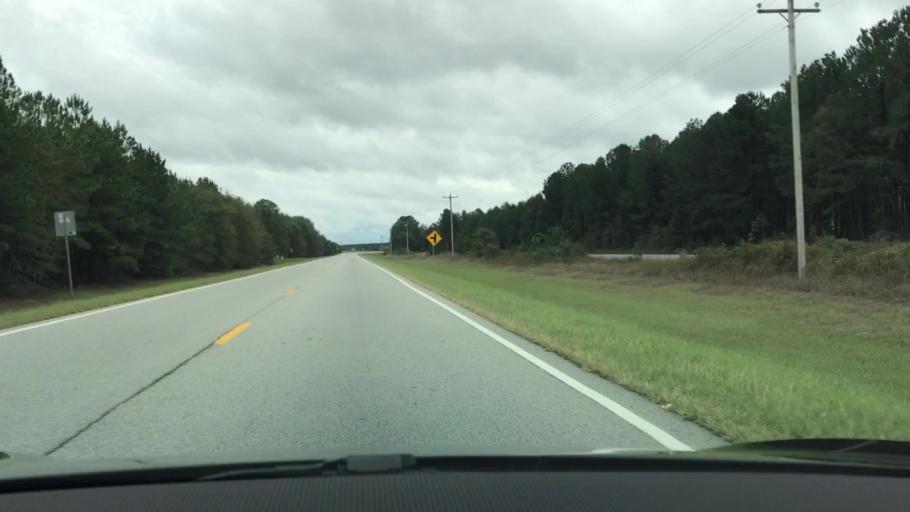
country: US
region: Georgia
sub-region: Glascock County
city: Gibson
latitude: 33.2993
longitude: -82.5176
